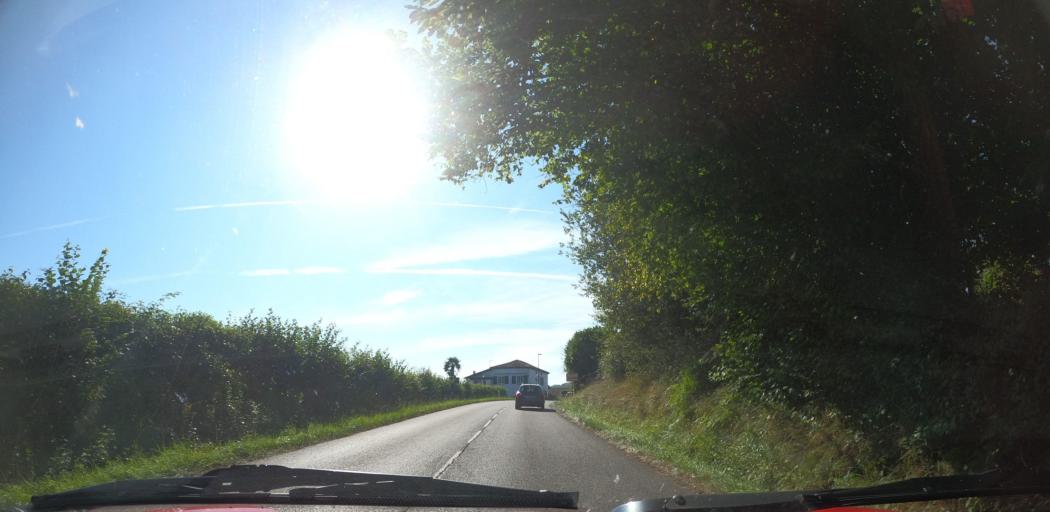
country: FR
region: Aquitaine
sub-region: Departement des Pyrenees-Atlantiques
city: Saint-Pee-sur-Nivelle
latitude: 43.3436
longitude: -1.5494
